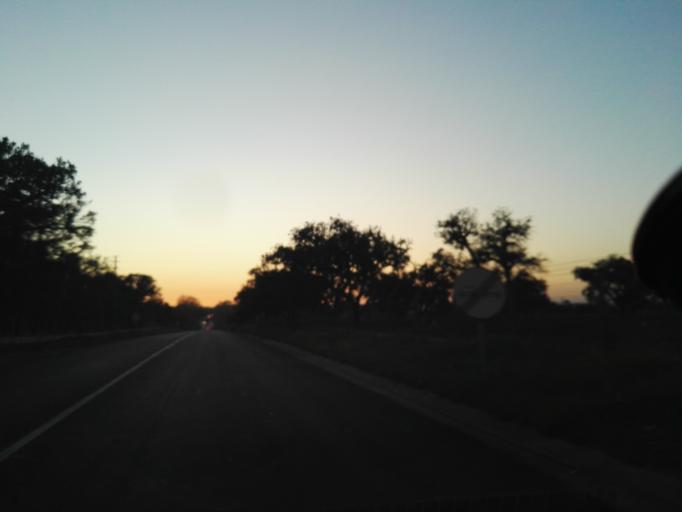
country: PT
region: Setubal
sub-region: Palmela
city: Pinhal Novo
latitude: 38.7100
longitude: -8.8889
